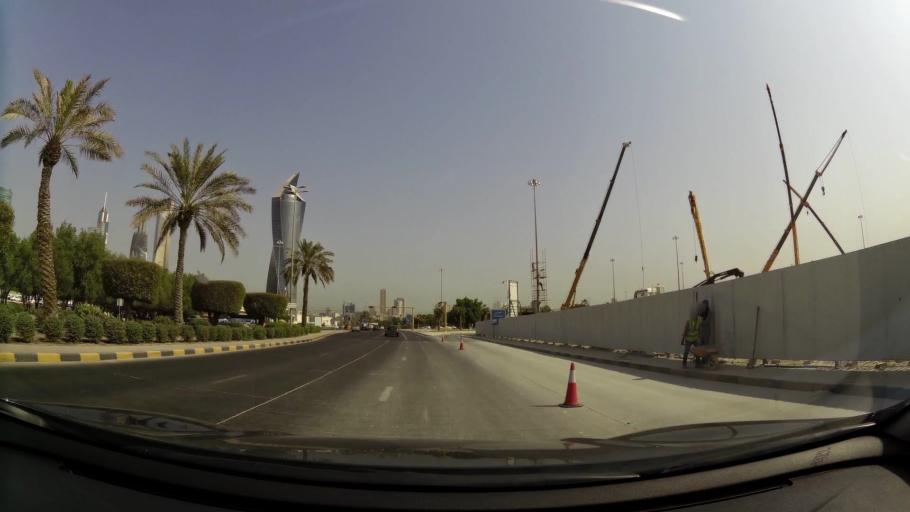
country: KW
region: Al Asimah
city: Kuwait City
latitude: 29.3654
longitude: 47.9892
